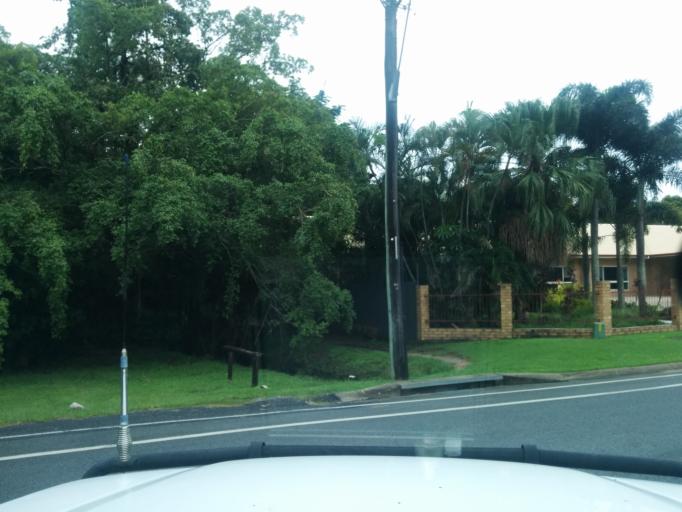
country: AU
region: Queensland
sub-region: Cairns
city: Cairns
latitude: -16.9200
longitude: 145.7539
